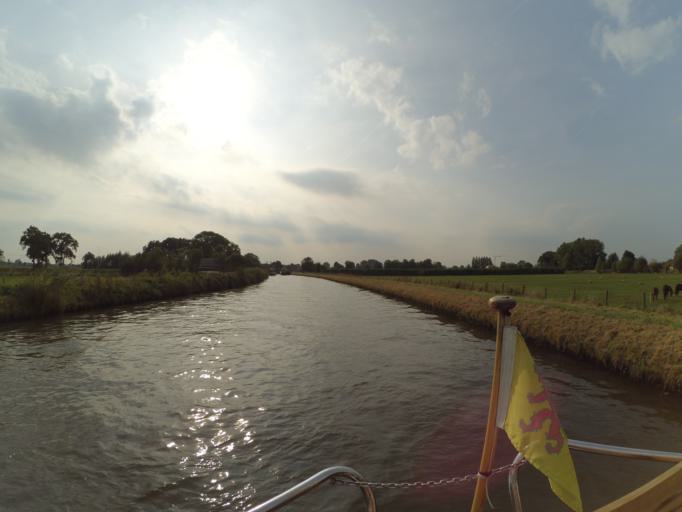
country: NL
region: Utrecht
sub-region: Gemeente IJsselstein
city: IJsselstein
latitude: 52.0543
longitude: 5.0098
